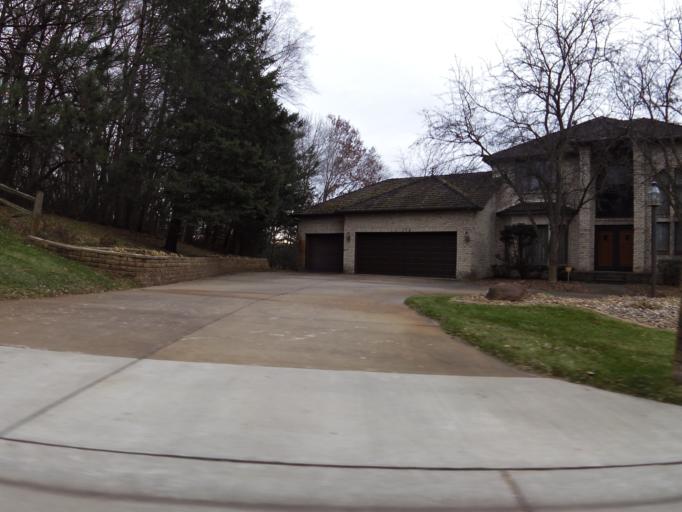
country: US
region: Minnesota
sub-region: Washington County
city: Lake Elmo
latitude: 44.9829
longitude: -92.8773
